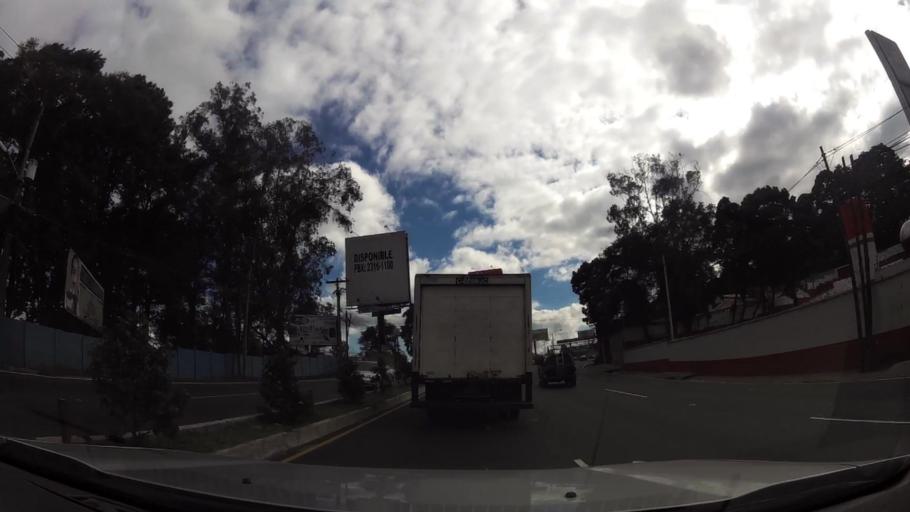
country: GT
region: Guatemala
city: Mixco
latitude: 14.6229
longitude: -90.6046
